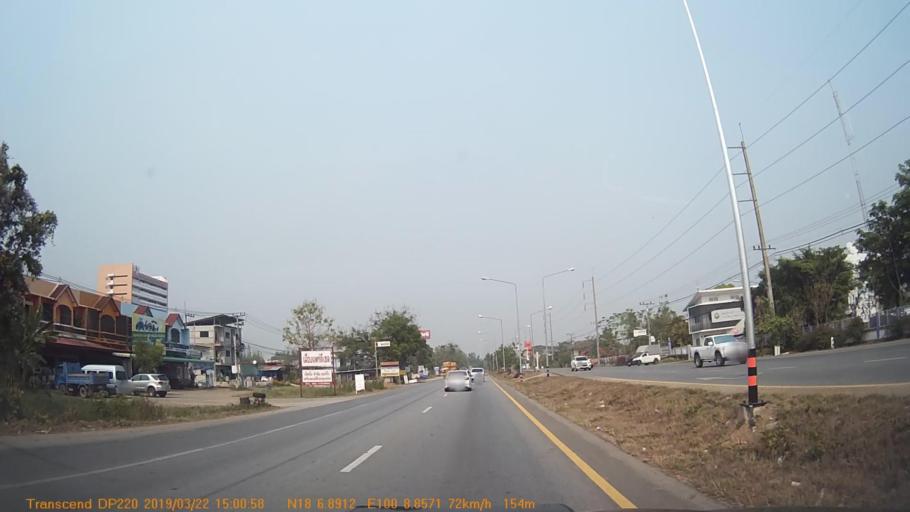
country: TH
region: Phrae
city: Phrae
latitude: 18.1151
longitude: 100.1480
